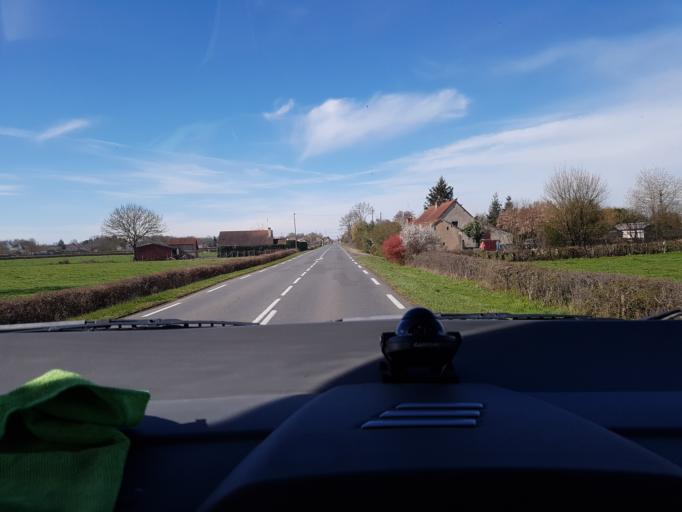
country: FR
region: Bourgogne
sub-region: Departement de Saone-et-Loire
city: Digoin
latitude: 46.5045
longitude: 4.0203
